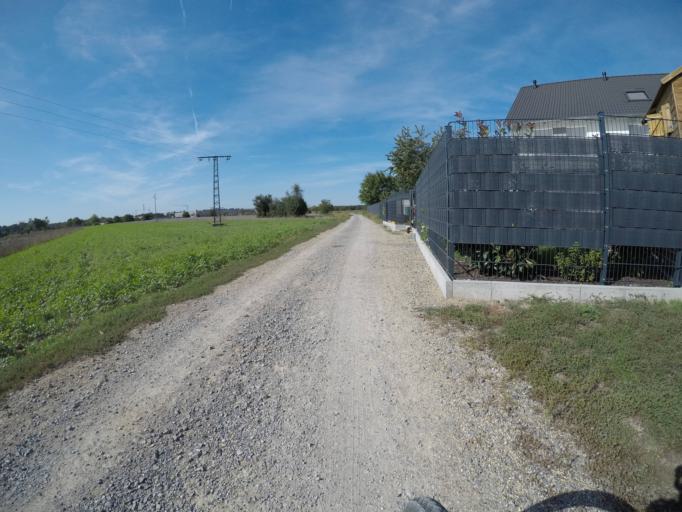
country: DE
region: Baden-Wuerttemberg
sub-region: Karlsruhe Region
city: Kronau
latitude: 49.2221
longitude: 8.6232
